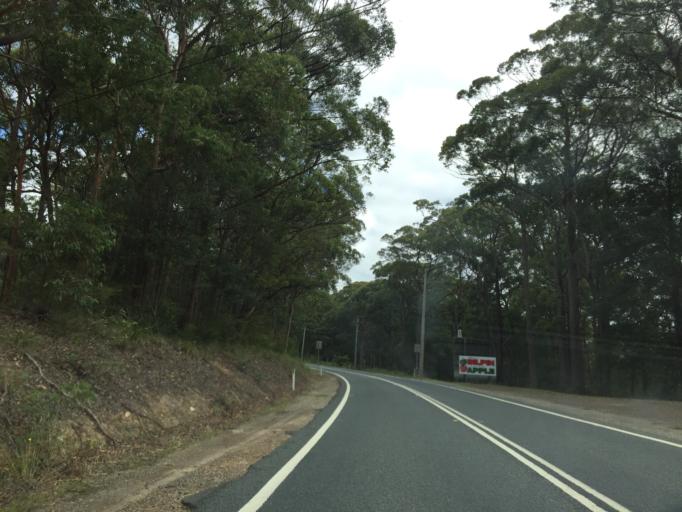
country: AU
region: New South Wales
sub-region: Hawkesbury
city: Richmond
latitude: -33.5165
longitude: 150.6127
